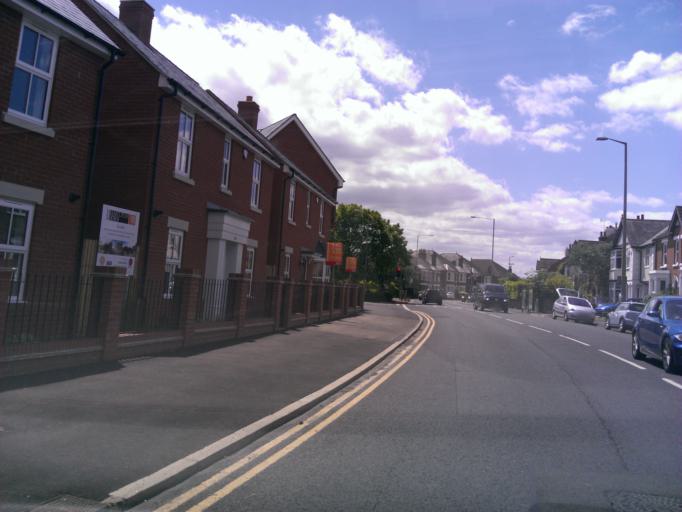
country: GB
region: England
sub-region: Essex
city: Colchester
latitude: 51.8800
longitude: 0.8791
